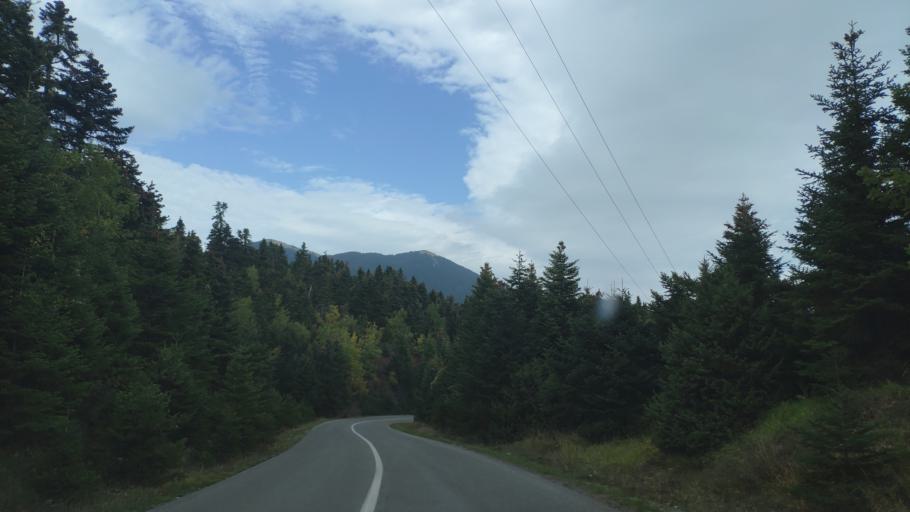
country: GR
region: Central Greece
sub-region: Nomos Fthiotidos
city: Stavros
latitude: 38.7181
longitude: 22.3268
